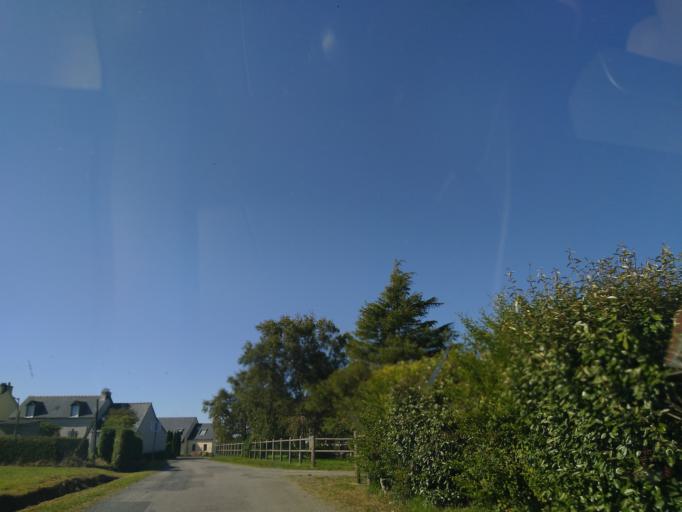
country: FR
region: Brittany
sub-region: Departement du Finistere
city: Le Faou
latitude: 48.2639
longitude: -4.1910
